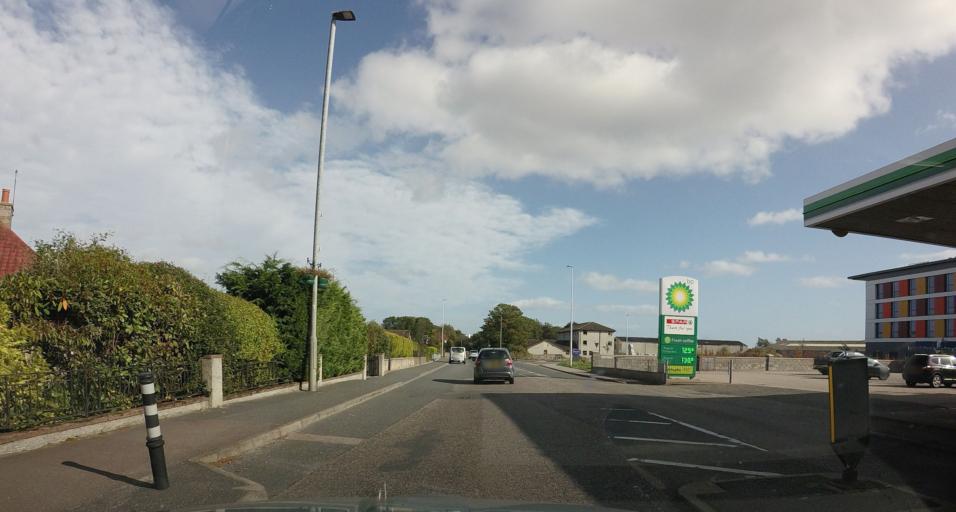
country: GB
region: Scotland
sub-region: Aberdeenshire
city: Westhill
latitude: 57.1497
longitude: -2.2957
